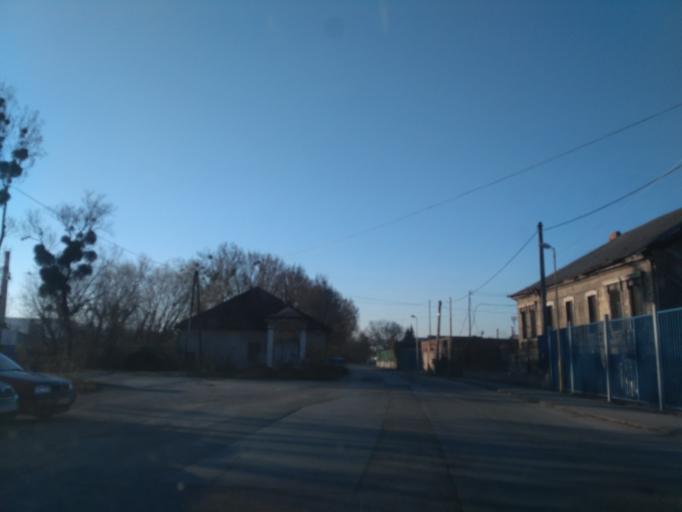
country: SK
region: Kosicky
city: Kosice
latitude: 48.7134
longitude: 21.2684
